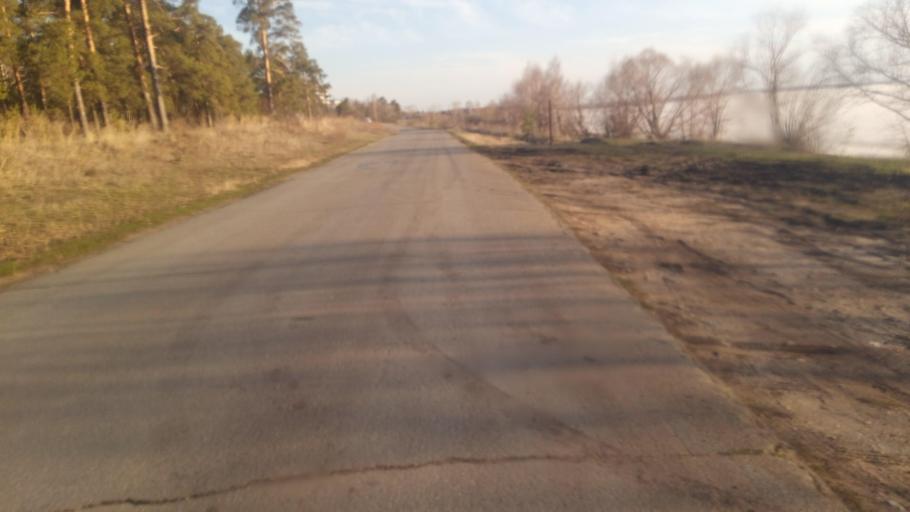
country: RU
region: Chelyabinsk
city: Novosineglazovskiy
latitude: 55.1292
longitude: 61.3281
